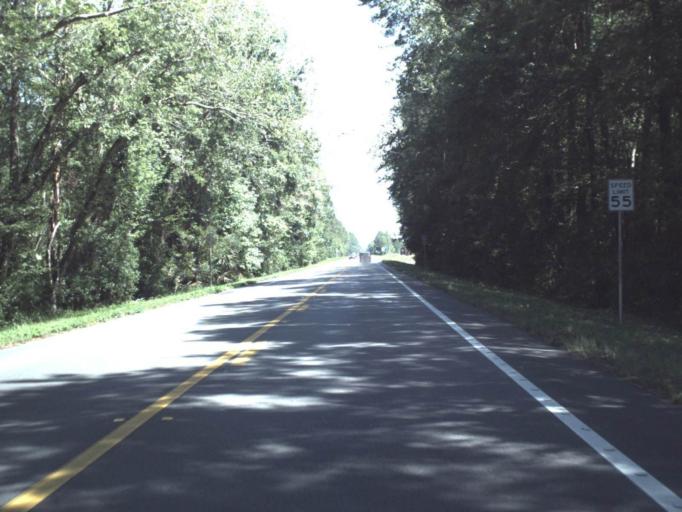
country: US
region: Florida
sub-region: Nassau County
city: Yulee
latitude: 30.7061
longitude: -81.6677
